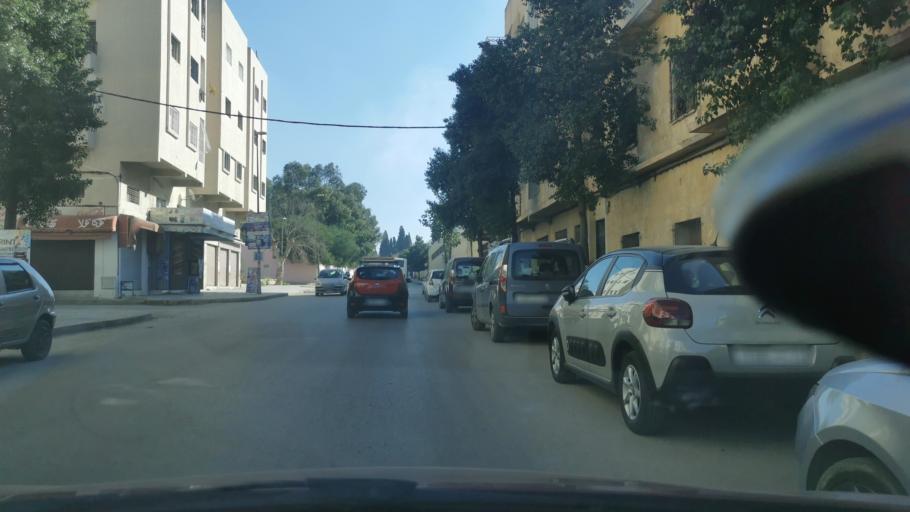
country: MA
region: Fes-Boulemane
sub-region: Fes
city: Fes
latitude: 34.0333
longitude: -4.9897
